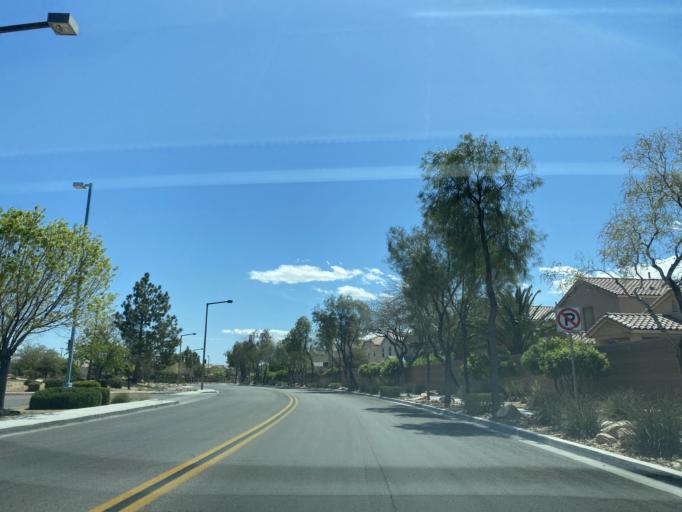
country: US
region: Nevada
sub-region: Clark County
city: North Las Vegas
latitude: 36.3187
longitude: -115.2120
